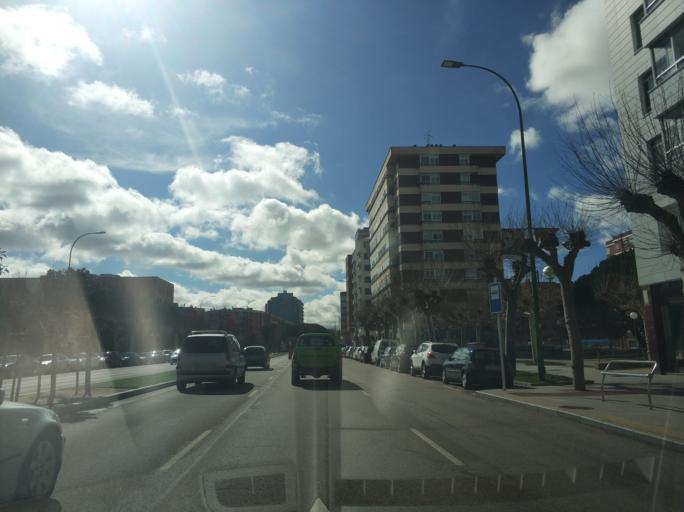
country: ES
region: Castille and Leon
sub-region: Provincia de Burgos
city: Burgos
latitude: 42.3482
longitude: -3.6883
